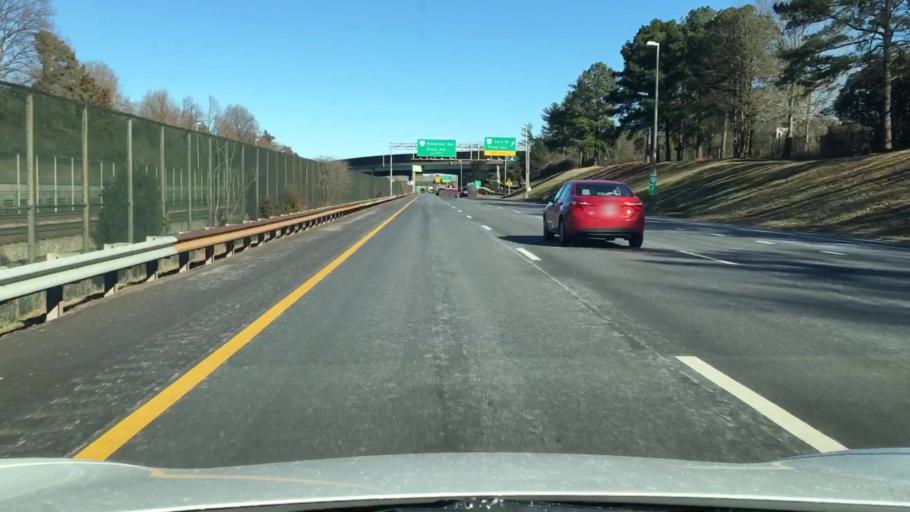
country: US
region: Virginia
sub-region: City of Richmond
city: Richmond
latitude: 37.5515
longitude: -77.4908
